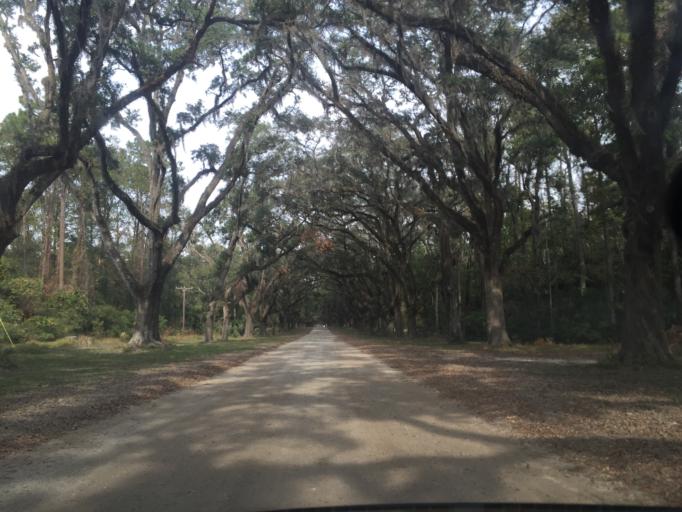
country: US
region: Georgia
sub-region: Chatham County
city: Isle of Hope
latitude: 31.9712
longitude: -81.0692
